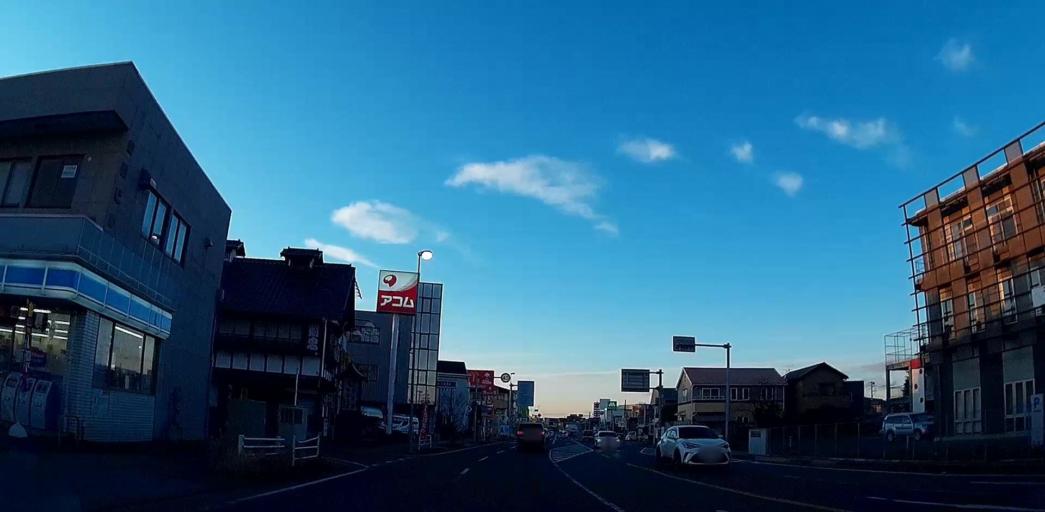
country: JP
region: Chiba
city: Katori-shi
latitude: 35.8965
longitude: 140.4989
